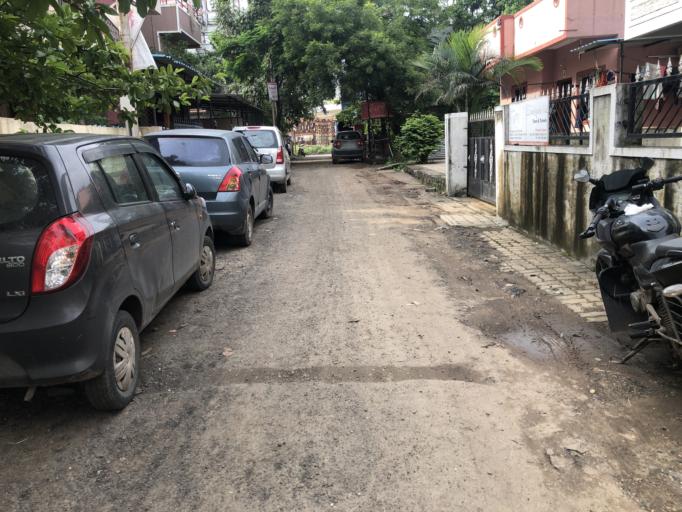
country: IN
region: Maharashtra
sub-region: Pune Division
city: Pimpri
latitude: 18.5911
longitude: 73.7852
